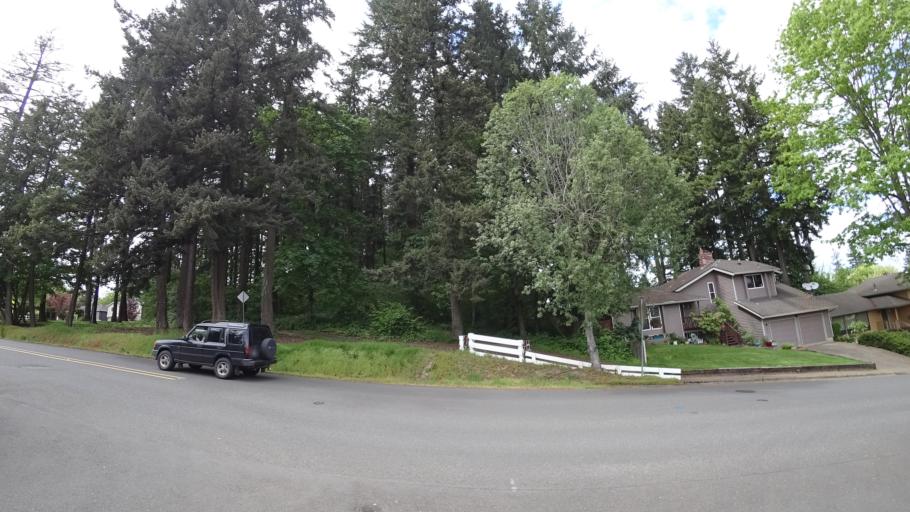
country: US
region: Oregon
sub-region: Washington County
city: Aloha
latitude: 45.4676
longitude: -122.8609
